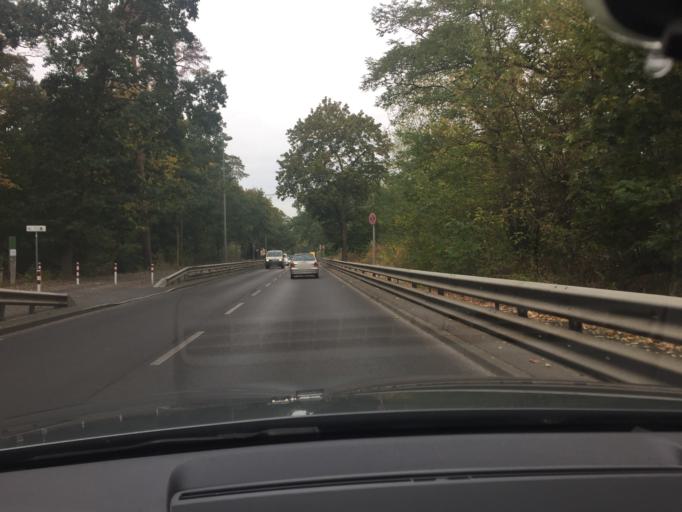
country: DE
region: Berlin
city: Rahnsdorf
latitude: 52.4444
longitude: 13.6806
